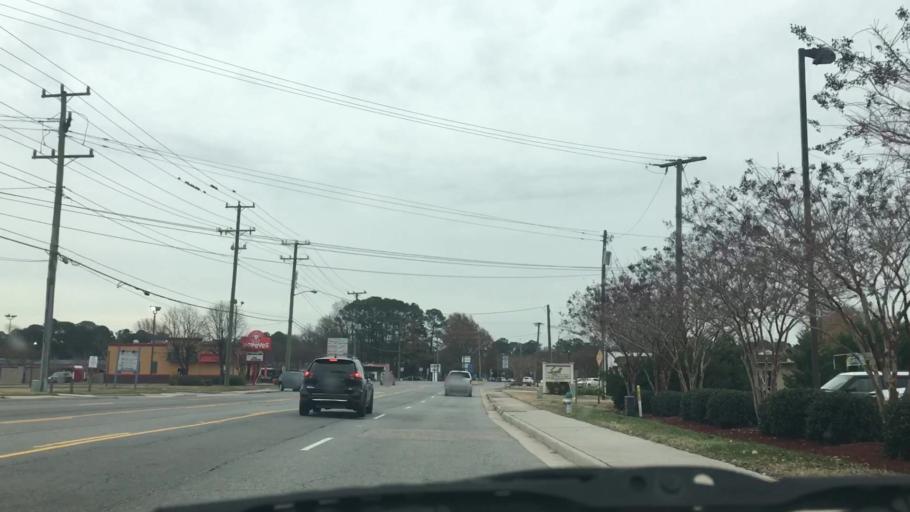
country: US
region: Virginia
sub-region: City of Portsmouth
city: Portsmouth Heights
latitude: 36.8623
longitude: -76.3936
